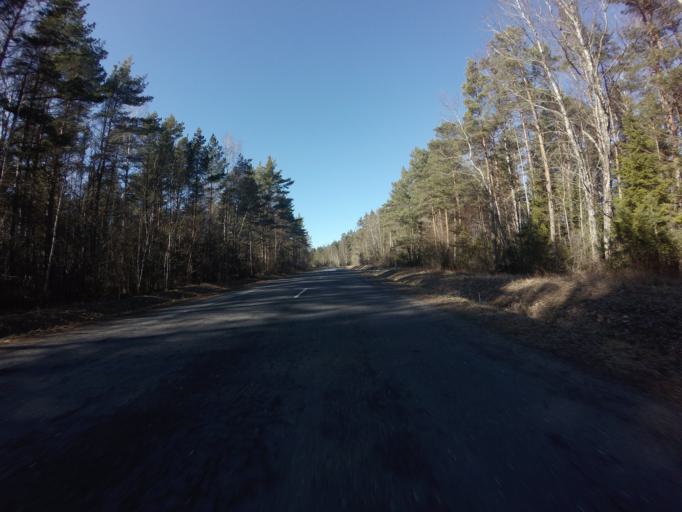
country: EE
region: Saare
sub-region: Kuressaare linn
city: Kuressaare
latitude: 58.5850
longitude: 22.6191
